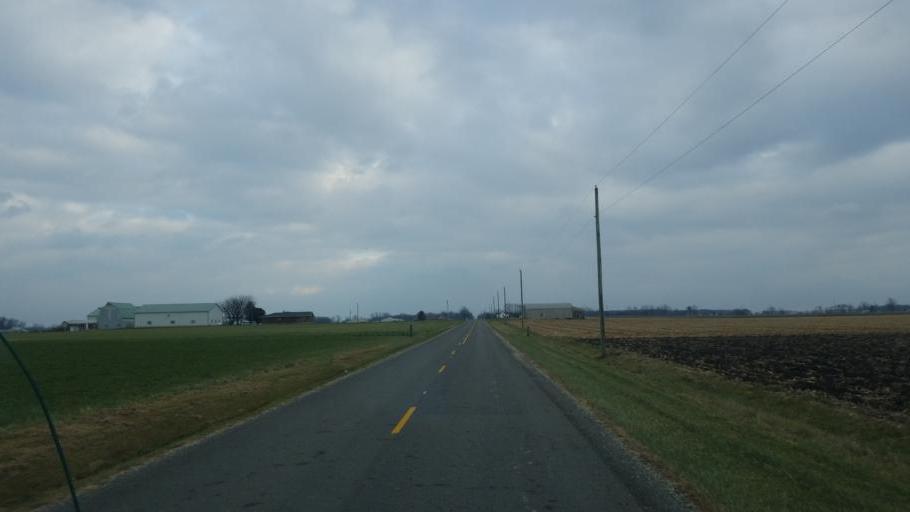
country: US
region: Ohio
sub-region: Mercer County
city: Coldwater
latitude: 40.5090
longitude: -84.6724
